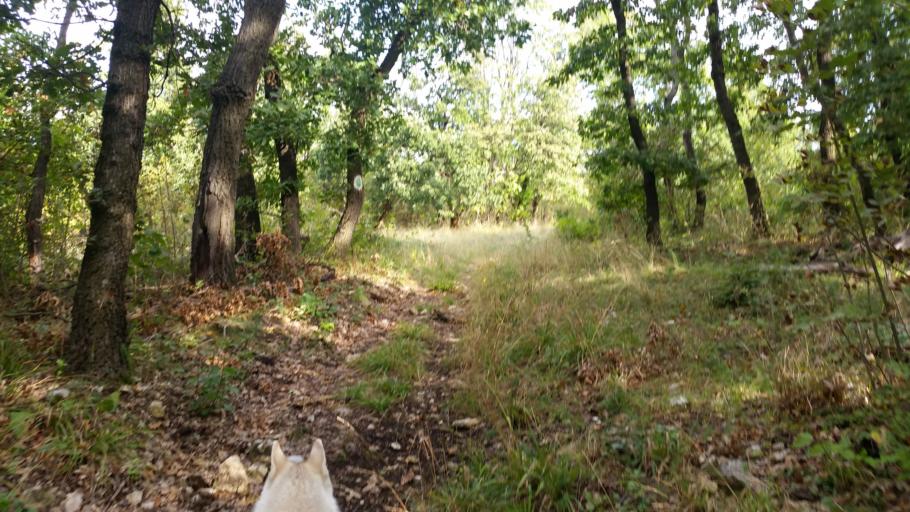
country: HU
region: Pest
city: Telki
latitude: 47.5641
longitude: 18.8303
